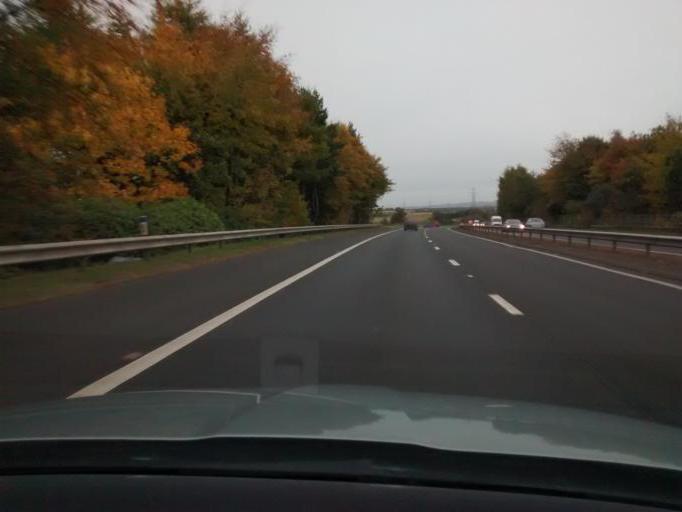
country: GB
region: Scotland
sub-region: Stirling
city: Plean
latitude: 56.0678
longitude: -3.8776
